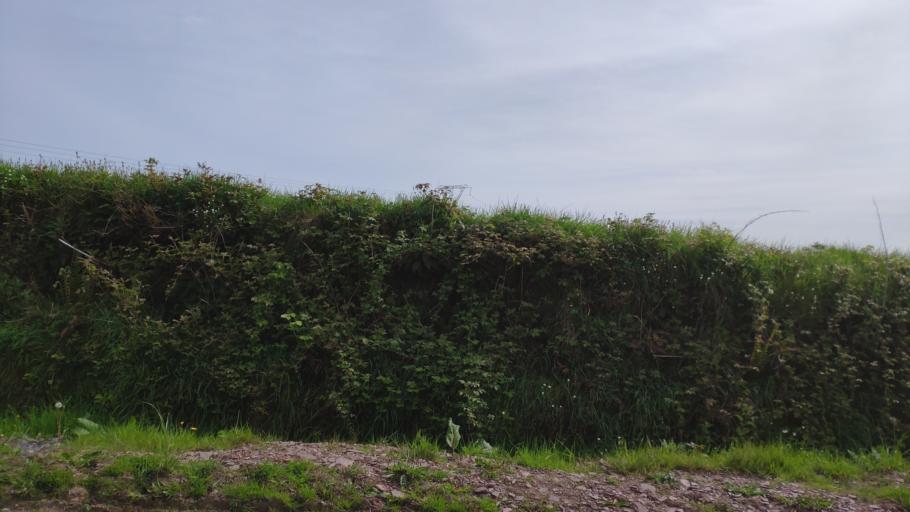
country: IE
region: Munster
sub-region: County Cork
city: Blarney
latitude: 51.9742
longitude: -8.5131
